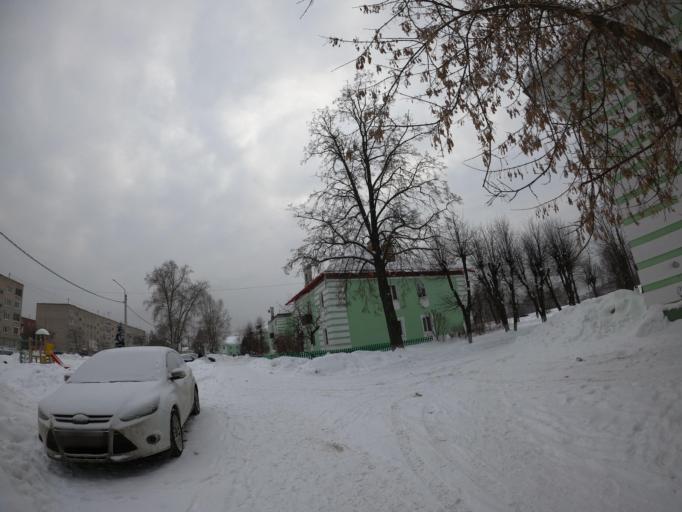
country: RU
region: Moskovskaya
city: Elektrogorsk
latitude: 55.8804
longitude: 38.7860
